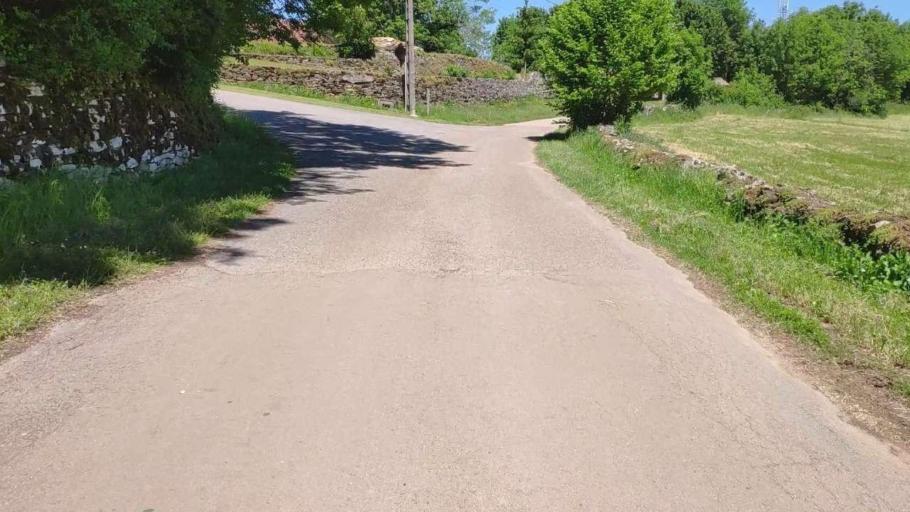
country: FR
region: Franche-Comte
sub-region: Departement du Jura
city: Perrigny
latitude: 46.7190
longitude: 5.6453
